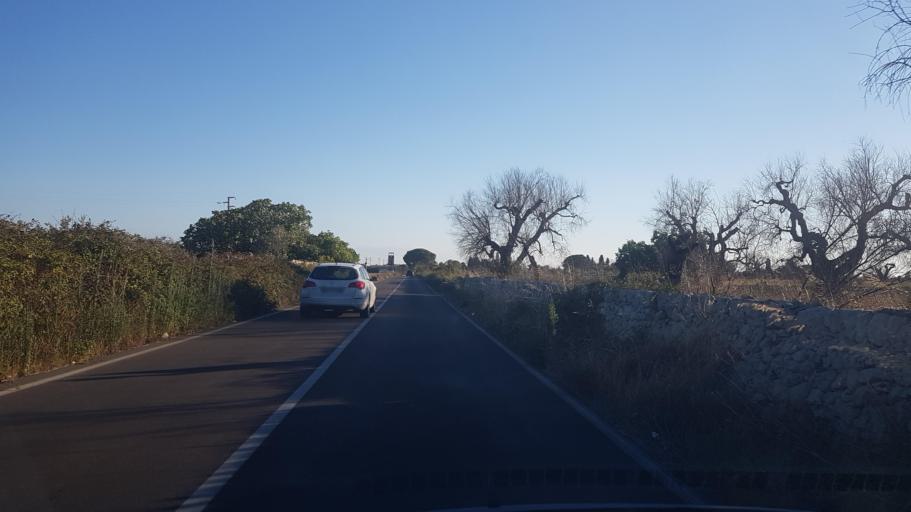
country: IT
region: Apulia
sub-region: Provincia di Lecce
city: Struda
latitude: 40.3316
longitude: 18.2929
